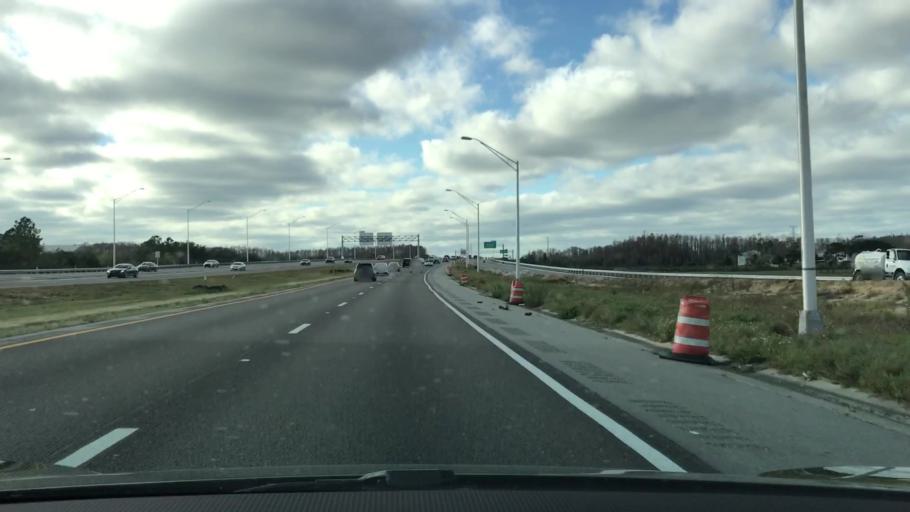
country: US
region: Florida
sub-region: Orange County
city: Southchase
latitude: 28.3690
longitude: -81.3940
